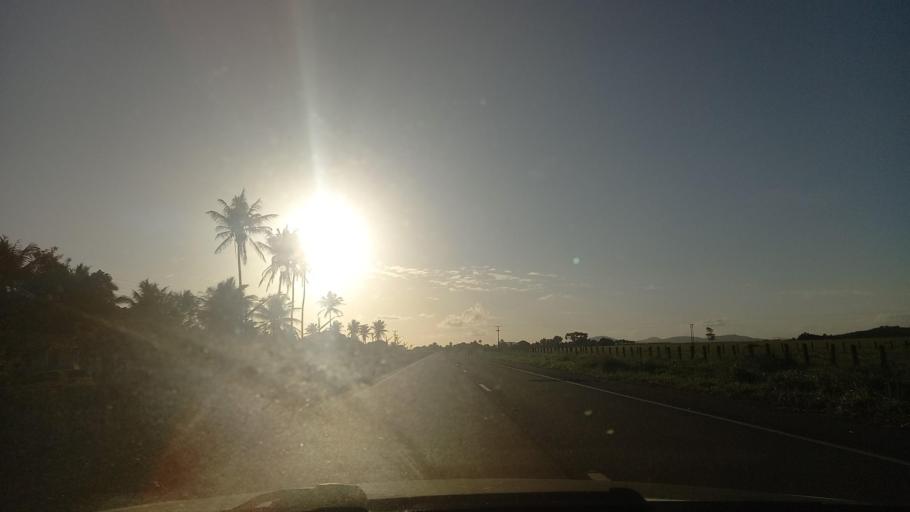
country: BR
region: Alagoas
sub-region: Limoeiro De Anadia
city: Cajueiro
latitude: -9.7458
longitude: -36.4620
